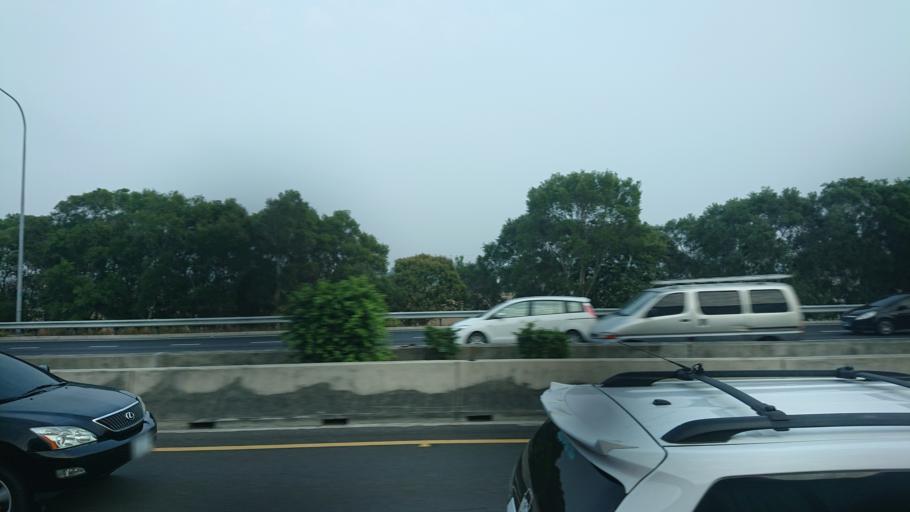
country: TW
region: Taiwan
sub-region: Chiayi
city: Jiayi Shi
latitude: 23.6169
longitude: 120.4379
